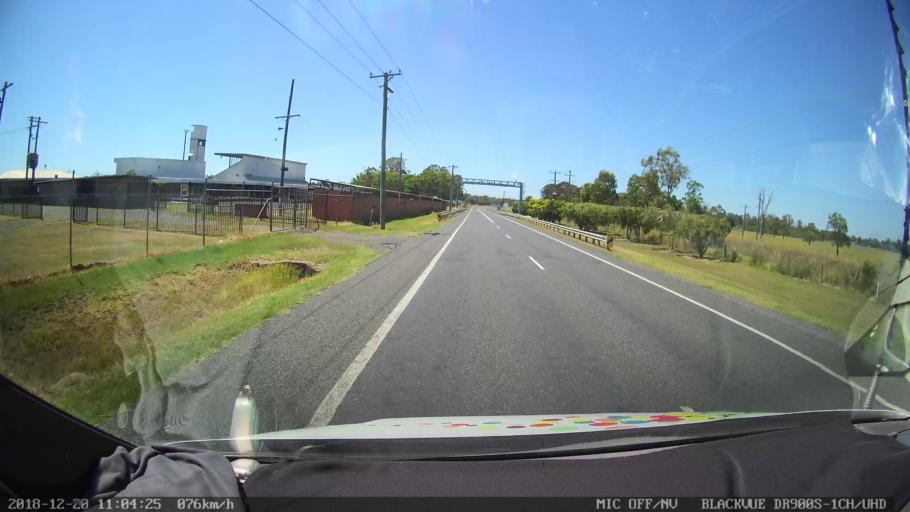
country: AU
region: New South Wales
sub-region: Richmond Valley
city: Casino
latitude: -28.8850
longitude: 153.0454
